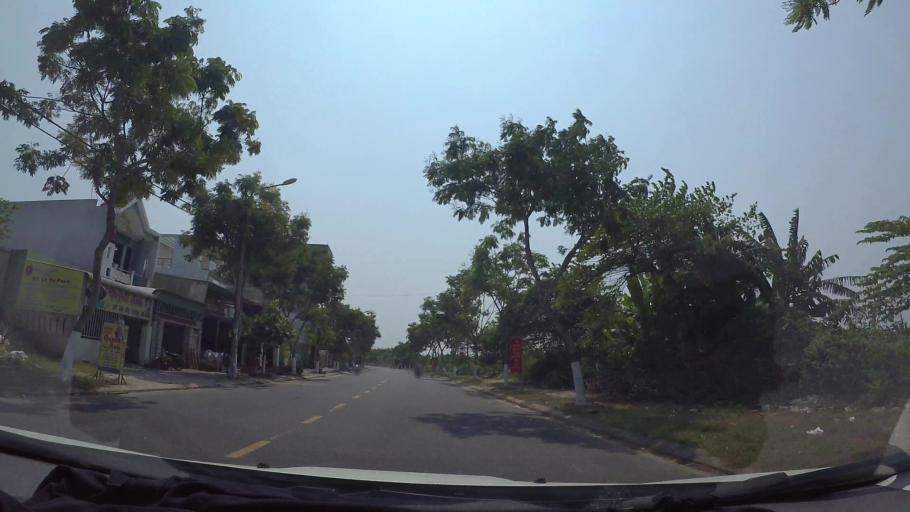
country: VN
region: Da Nang
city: Cam Le
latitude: 16.0009
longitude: 108.2033
